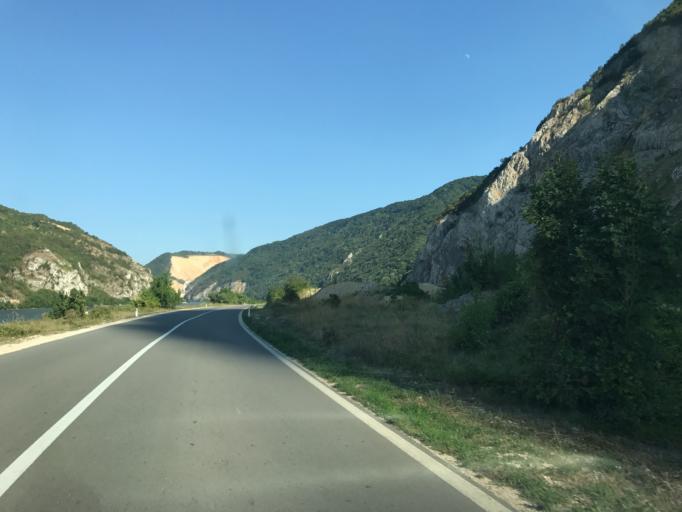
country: RO
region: Caras-Severin
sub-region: Comuna Pescari
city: Coronini
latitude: 44.6608
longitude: 21.6989
